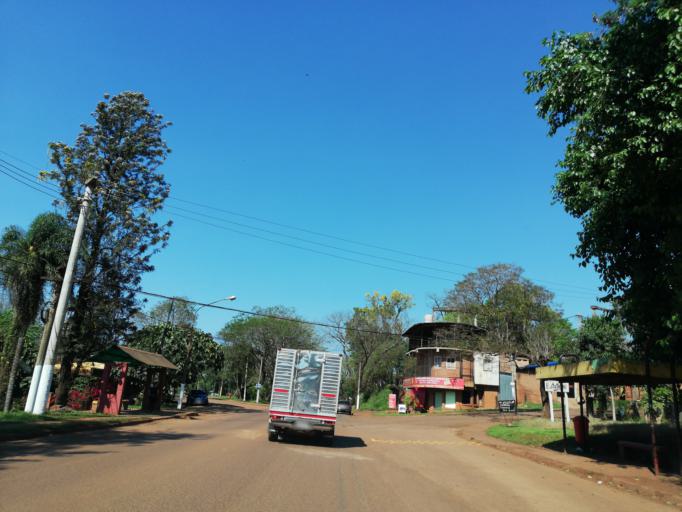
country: AR
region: Misiones
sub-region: Departamento de Eldorado
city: Eldorado
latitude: -26.4064
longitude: -54.6406
